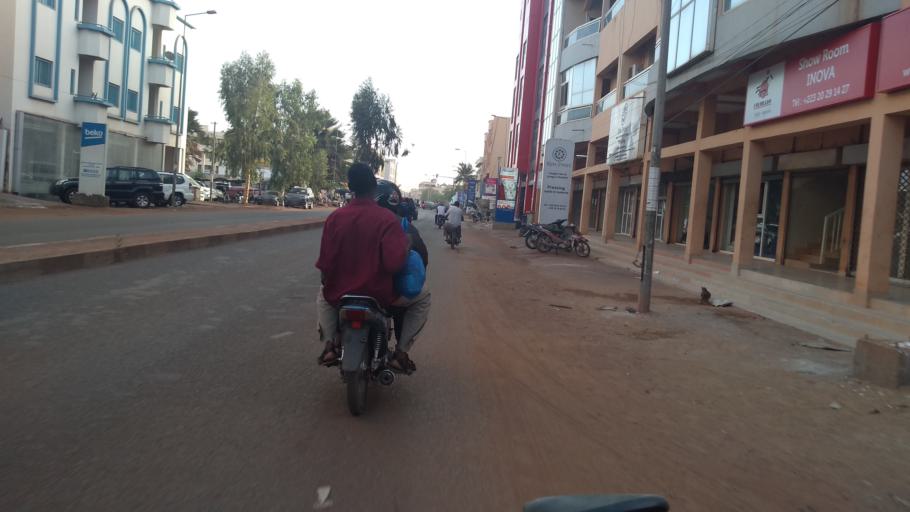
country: ML
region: Bamako
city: Bamako
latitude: 12.6278
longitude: -8.0332
